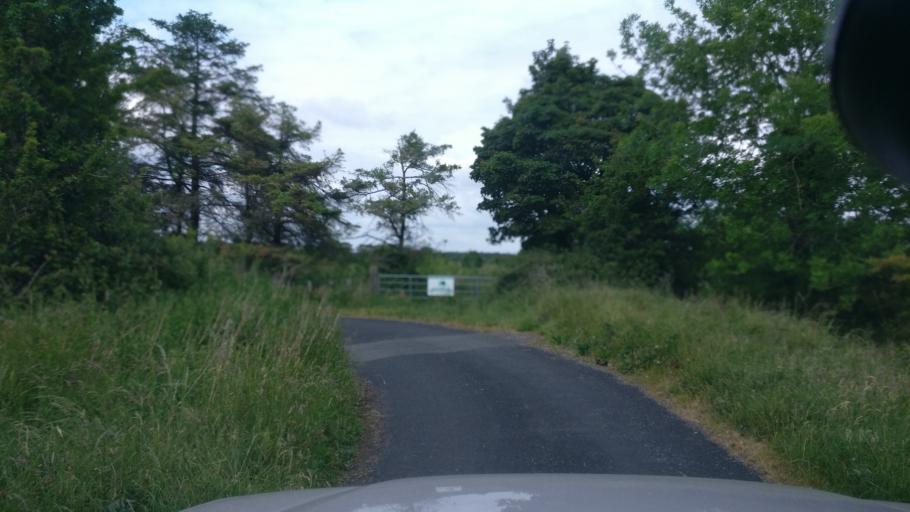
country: IE
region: Connaught
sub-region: County Galway
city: Ballinasloe
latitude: 53.2714
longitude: -8.3610
